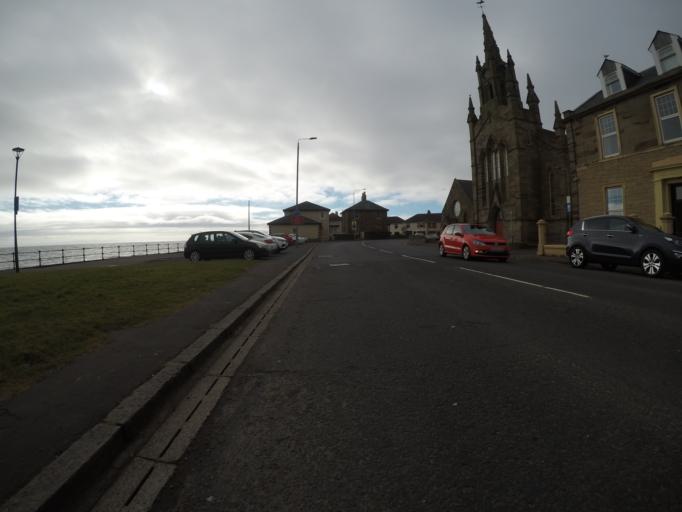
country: GB
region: Scotland
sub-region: North Ayrshire
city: Ardrossan
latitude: 55.6395
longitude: -4.8104
